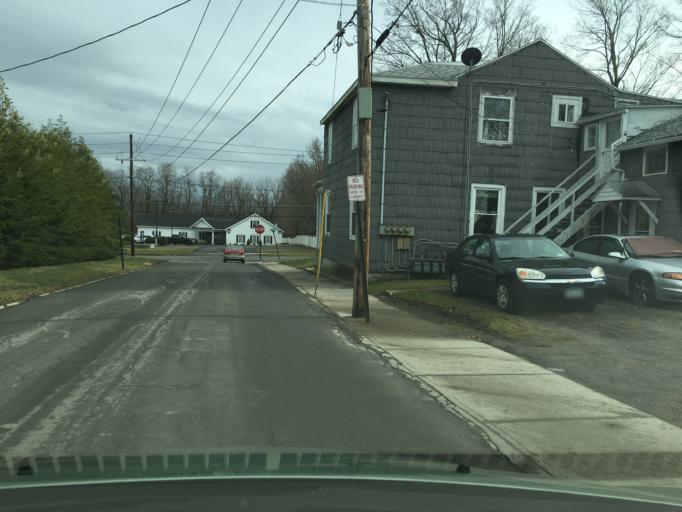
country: US
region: New York
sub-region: Wyoming County
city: Perry
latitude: 42.7223
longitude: -77.9990
